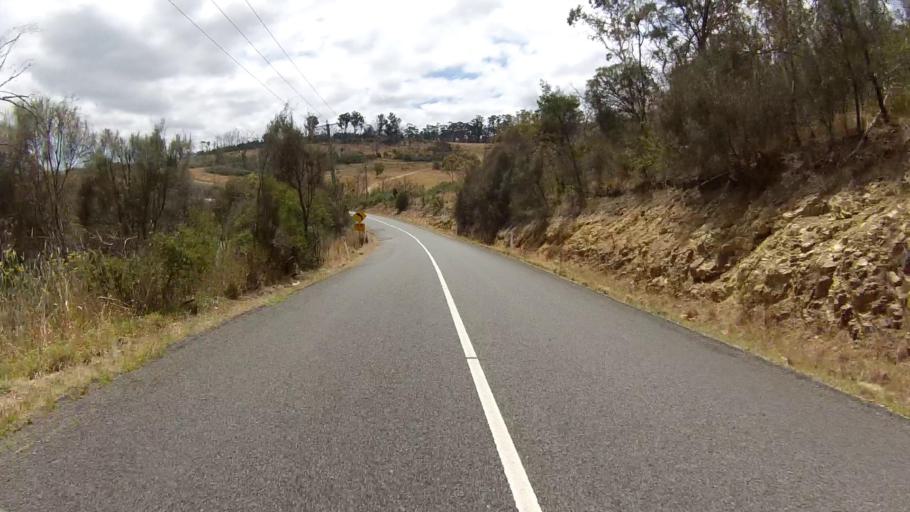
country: AU
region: Tasmania
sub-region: Sorell
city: Sorell
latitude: -42.8646
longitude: 147.6913
